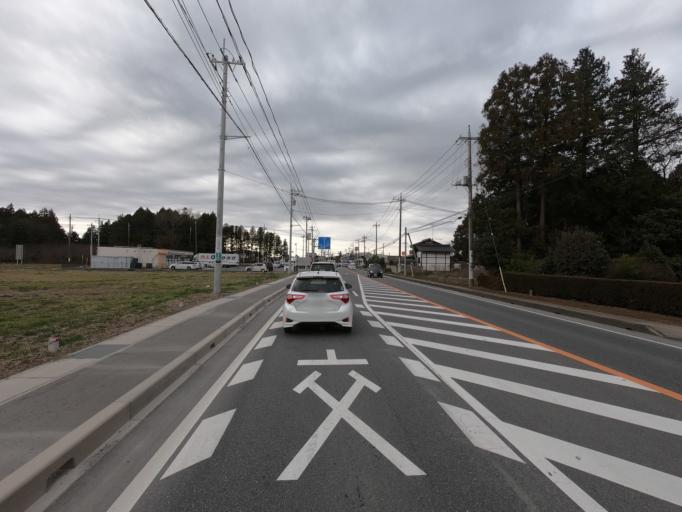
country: JP
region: Ibaraki
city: Ishioka
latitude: 36.0985
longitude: 140.2778
